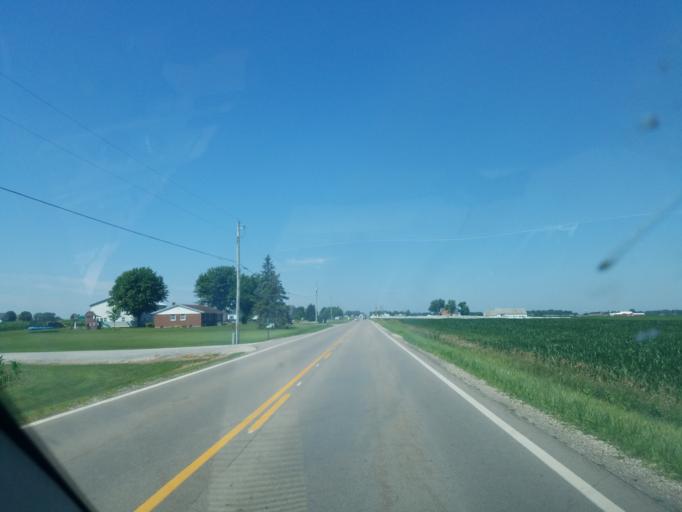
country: US
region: Ohio
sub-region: Auglaize County
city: Minster
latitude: 40.4076
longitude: -84.4500
